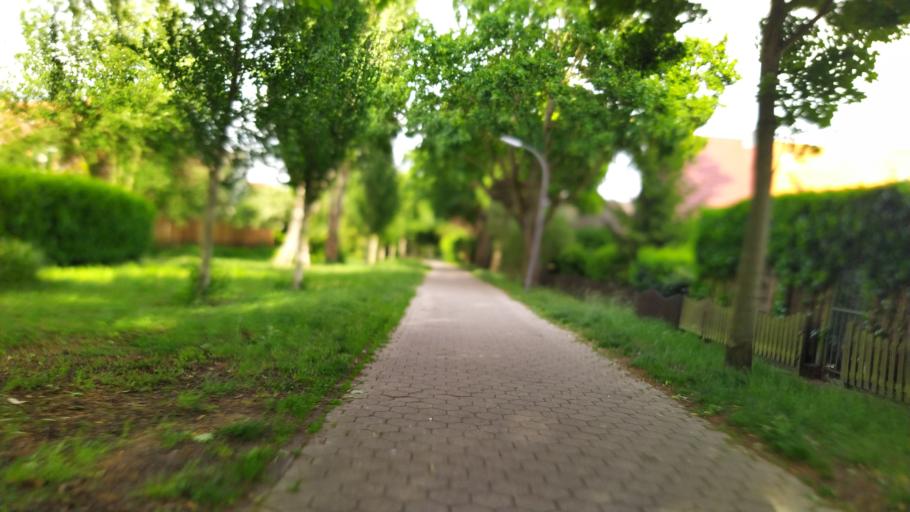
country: DE
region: Hamburg
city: Altona
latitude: 53.4804
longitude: 9.8862
